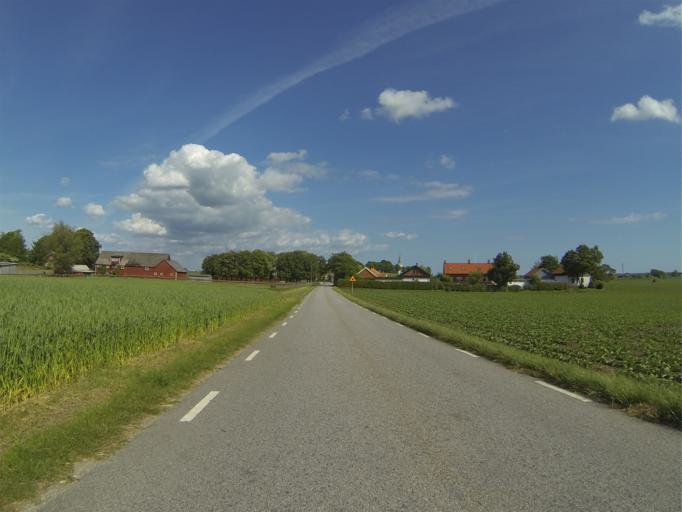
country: SE
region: Skane
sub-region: Staffanstorps Kommun
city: Hjaerup
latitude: 55.6316
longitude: 13.1341
